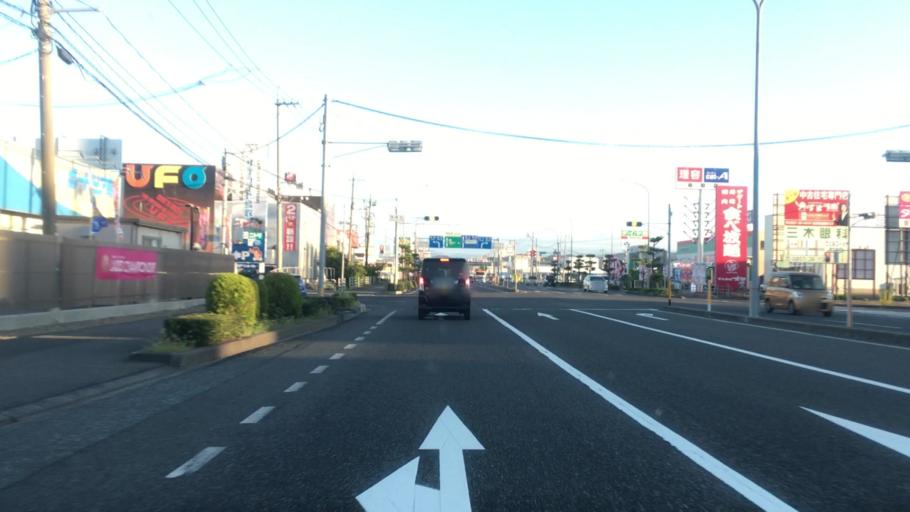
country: JP
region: Tottori
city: Tottori
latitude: 35.5212
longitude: 134.2026
